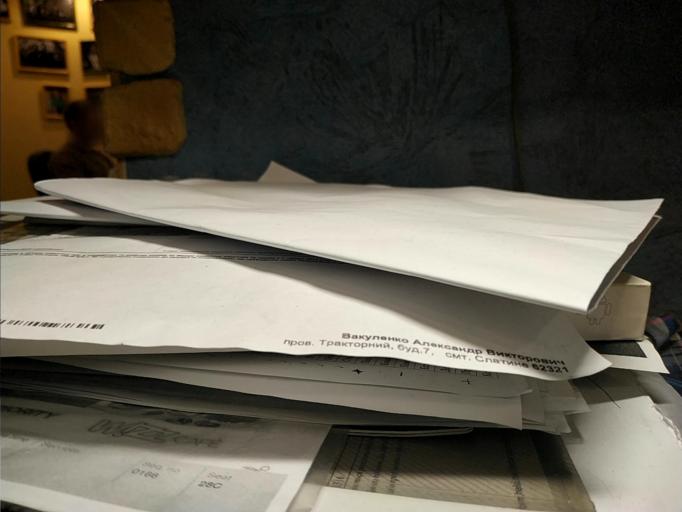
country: RU
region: Tverskaya
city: Zubtsov
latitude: 56.1068
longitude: 34.6499
